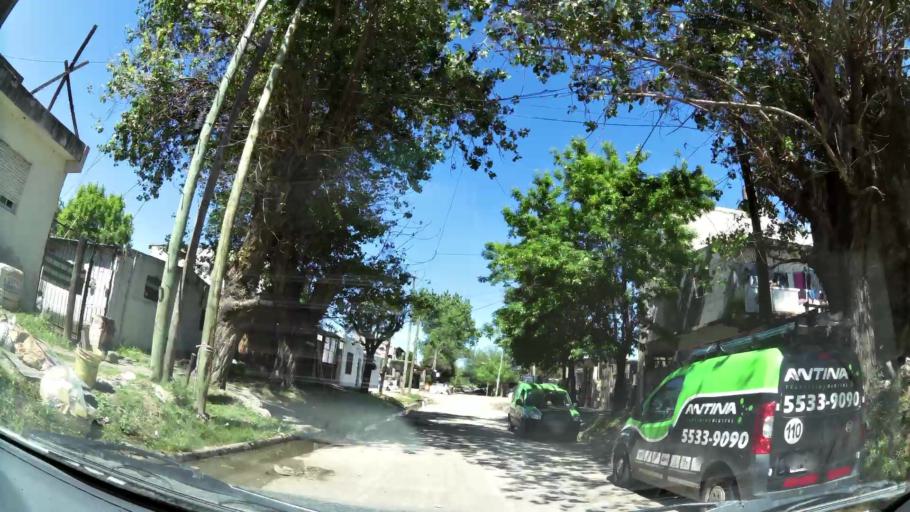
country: AR
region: Buenos Aires
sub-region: Partido de Quilmes
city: Quilmes
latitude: -34.7274
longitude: -58.3124
